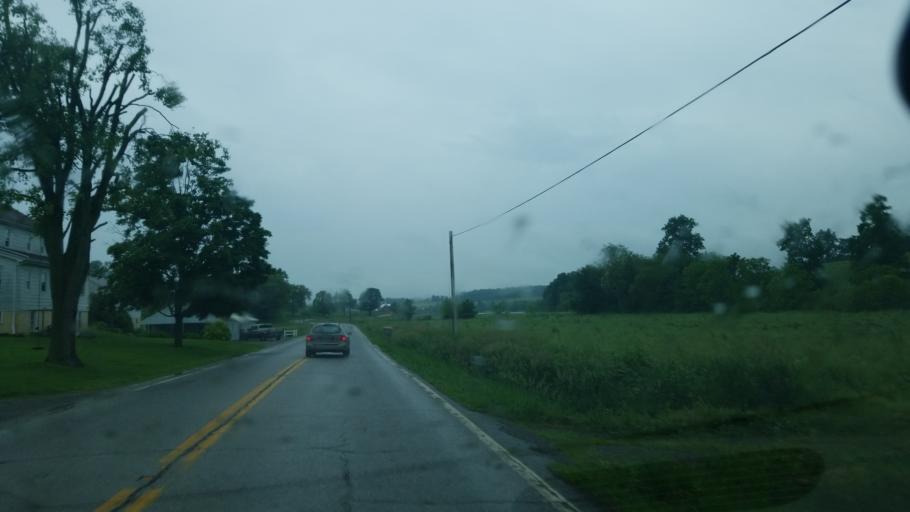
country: US
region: Ohio
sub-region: Tuscarawas County
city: Sugarcreek
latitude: 40.4760
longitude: -81.7150
